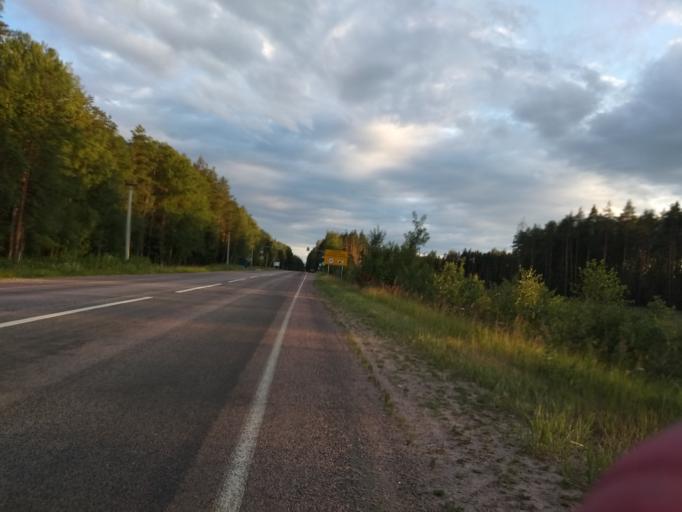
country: RU
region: Moskovskaya
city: Misheronskiy
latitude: 55.6196
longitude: 39.7275
